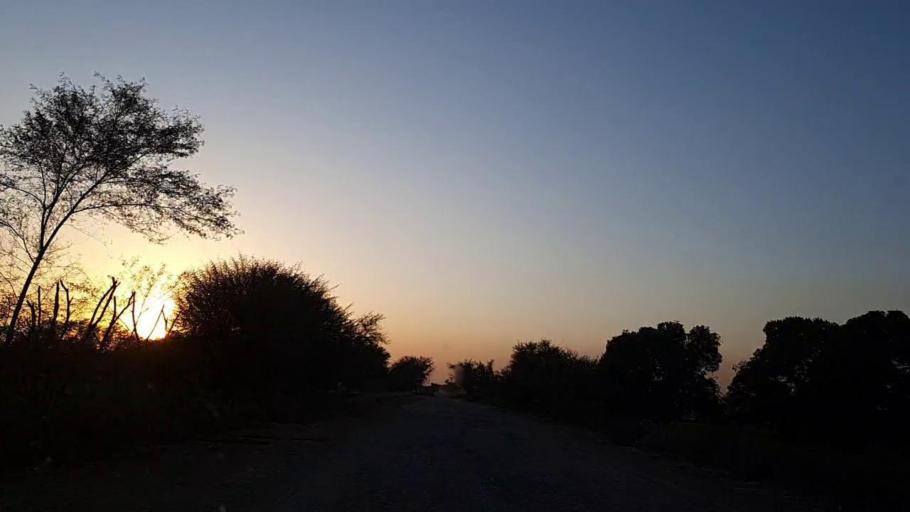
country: PK
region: Sindh
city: Daur
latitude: 26.3504
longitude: 68.3212
